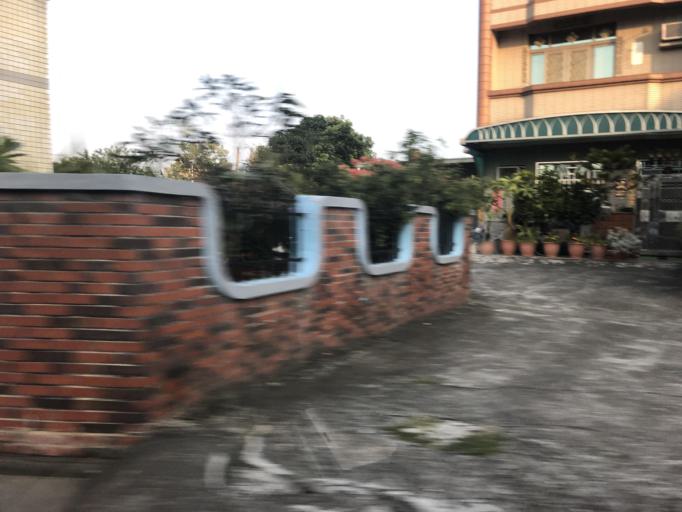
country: TW
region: Taiwan
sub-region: Tainan
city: Tainan
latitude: 23.1447
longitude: 120.2692
